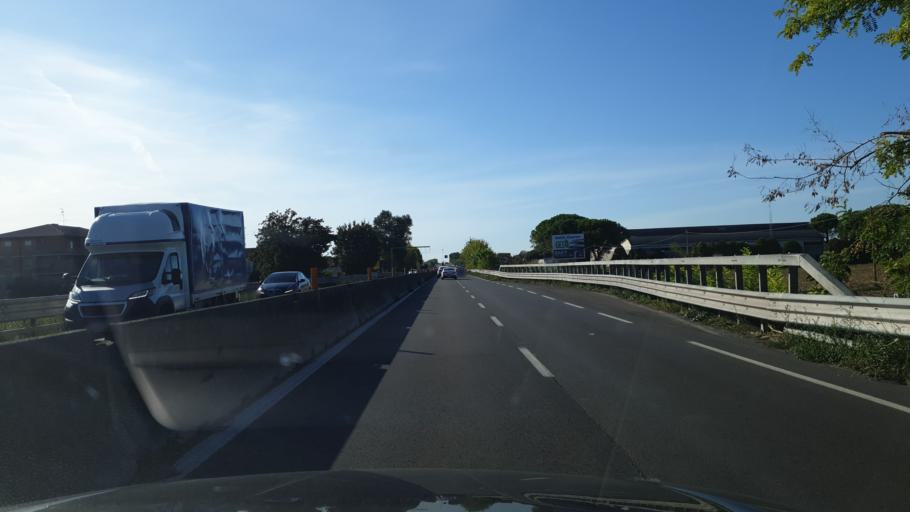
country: IT
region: Emilia-Romagna
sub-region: Provincia di Ravenna
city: Madonna Dell'Albero
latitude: 44.3810
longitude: 12.2054
